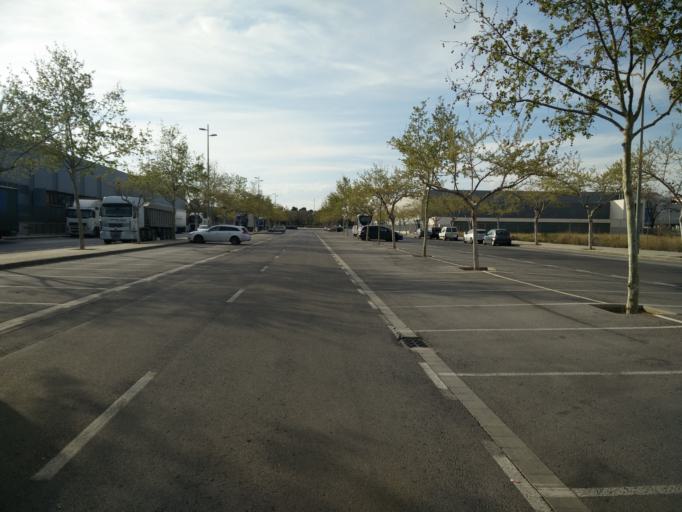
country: ES
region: Valencia
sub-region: Provincia de Castello
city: Castello de la Plana
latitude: 39.9803
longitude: -0.0619
